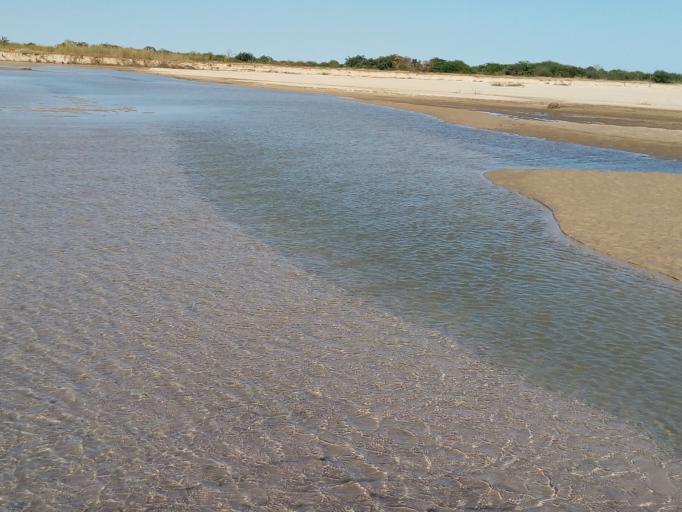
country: MG
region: Menabe
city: Morondava
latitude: -20.3390
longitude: 44.3097
